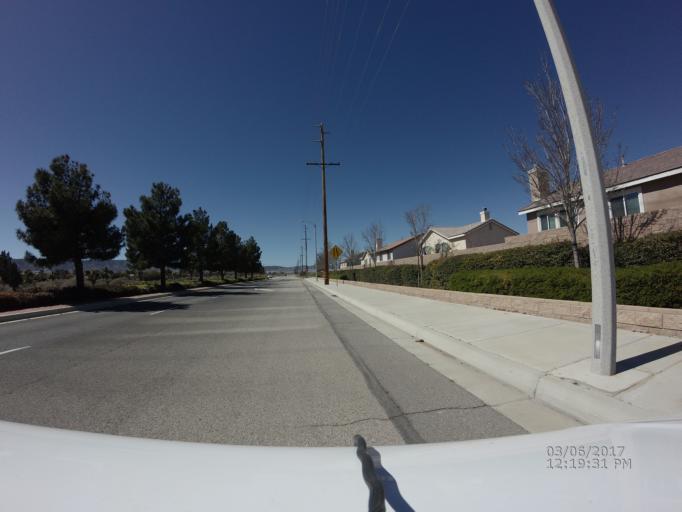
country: US
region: California
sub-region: Los Angeles County
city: Quartz Hill
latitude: 34.6750
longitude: -118.2157
